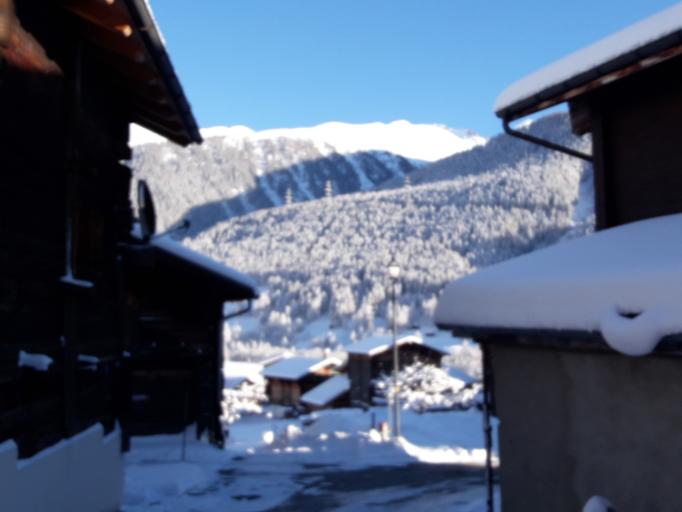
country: CH
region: Valais
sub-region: Goms District
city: Fiesch
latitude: 46.4653
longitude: 8.2308
